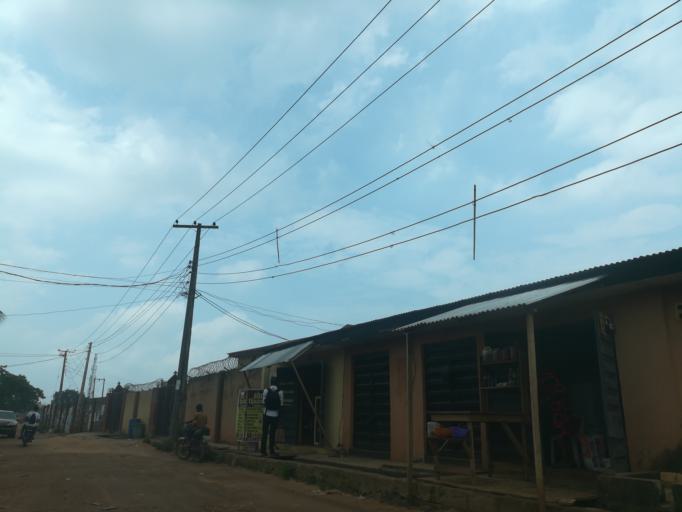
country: NG
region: Lagos
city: Ikorodu
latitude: 6.6161
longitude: 3.5218
